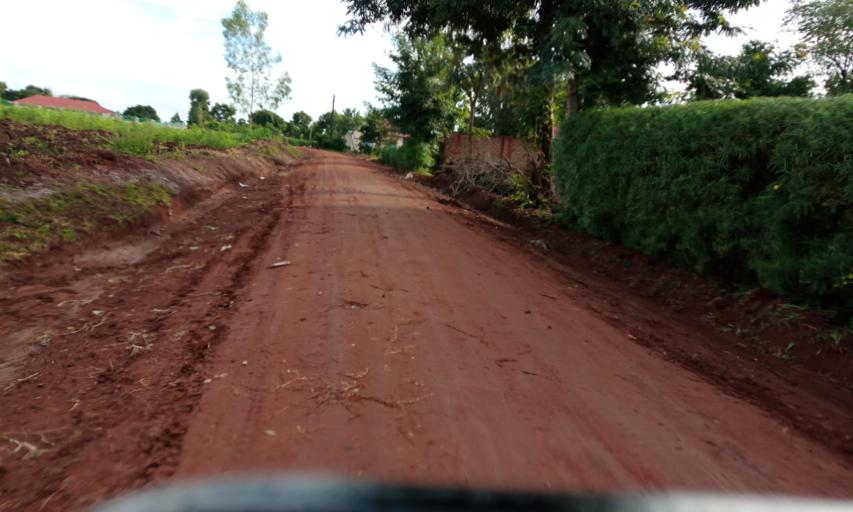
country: UG
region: Eastern Region
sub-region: Mbale District
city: Mbale
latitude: 1.1402
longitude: 34.1689
